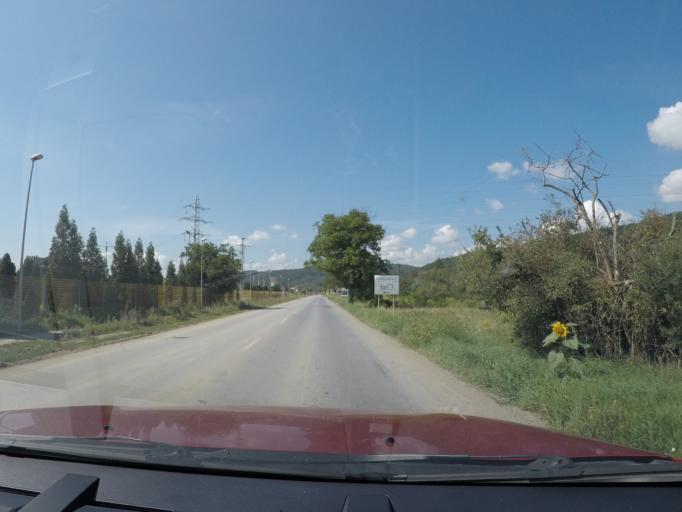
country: SK
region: Presovsky
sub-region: Okres Presov
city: Presov
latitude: 48.9662
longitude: 21.2484
